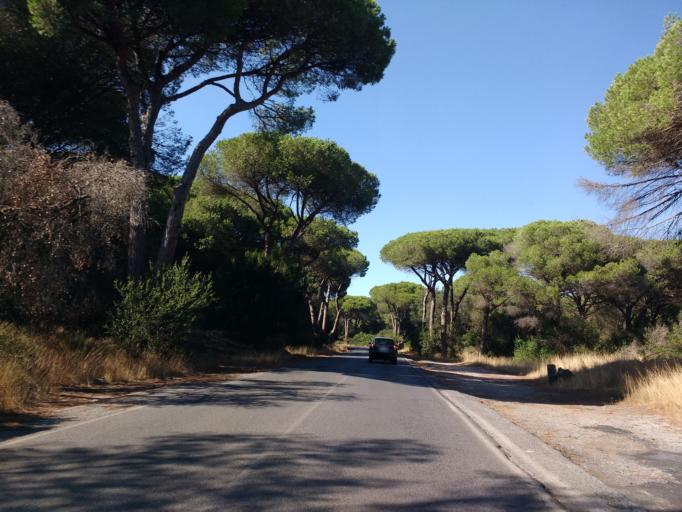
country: IT
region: Latium
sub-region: Citta metropolitana di Roma Capitale
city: Acilia-Castel Fusano-Ostia Antica
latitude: 41.7106
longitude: 12.3579
